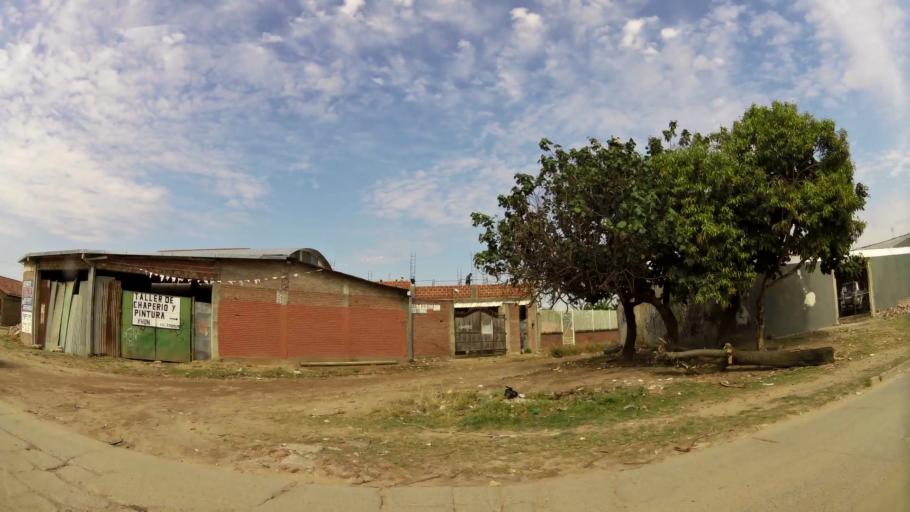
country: BO
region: Santa Cruz
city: Santa Cruz de la Sierra
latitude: -17.7366
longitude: -63.1370
